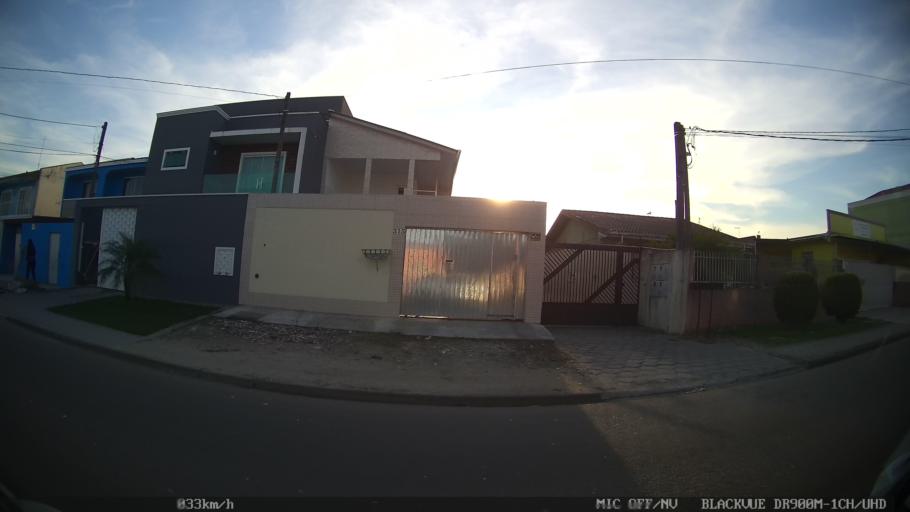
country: BR
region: Parana
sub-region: Pinhais
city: Pinhais
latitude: -25.4484
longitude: -49.1748
